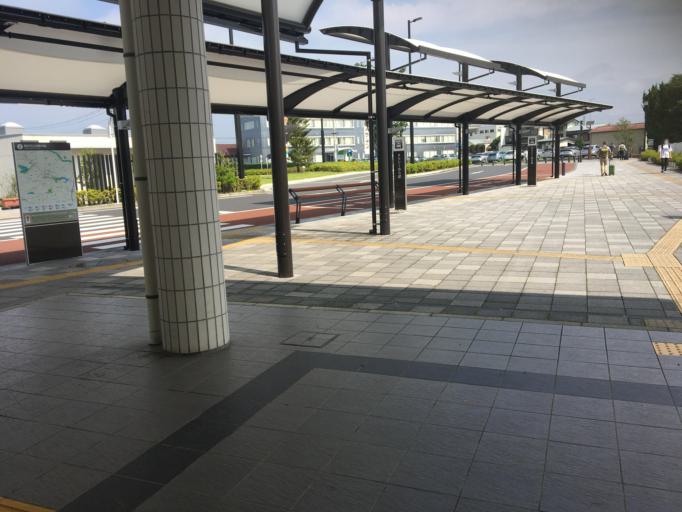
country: JP
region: Gunma
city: Tatebayashi
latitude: 36.2466
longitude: 139.5273
